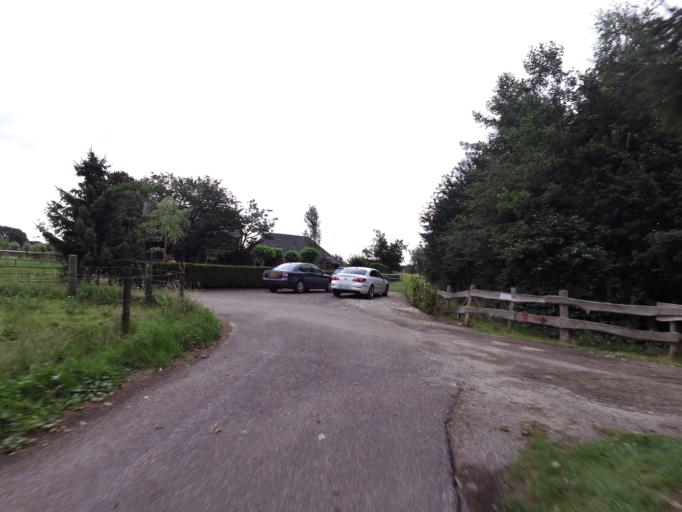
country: NL
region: Gelderland
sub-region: Gemeente Doesburg
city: Doesburg
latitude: 51.9651
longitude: 6.1991
